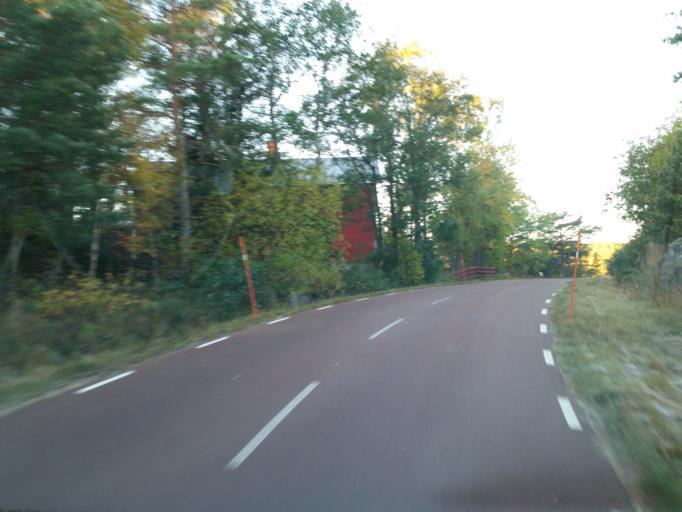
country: AX
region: Alands skaergard
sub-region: Vardoe
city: Vardoe
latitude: 60.3465
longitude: 20.3373
